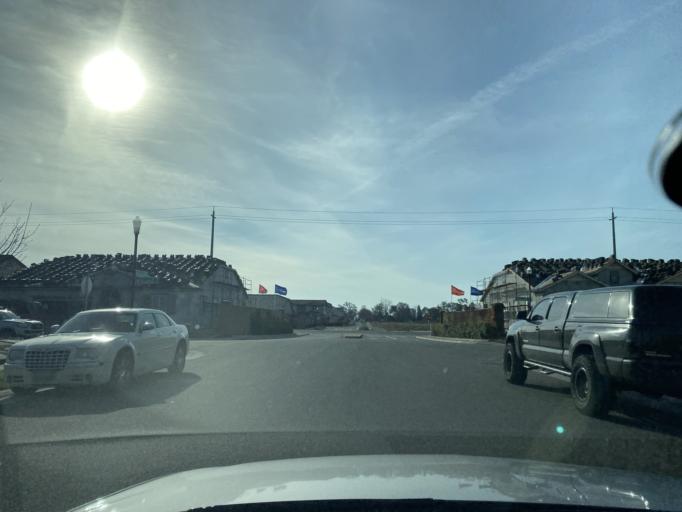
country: US
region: California
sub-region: Sacramento County
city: Elk Grove
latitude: 38.3953
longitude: -121.3878
